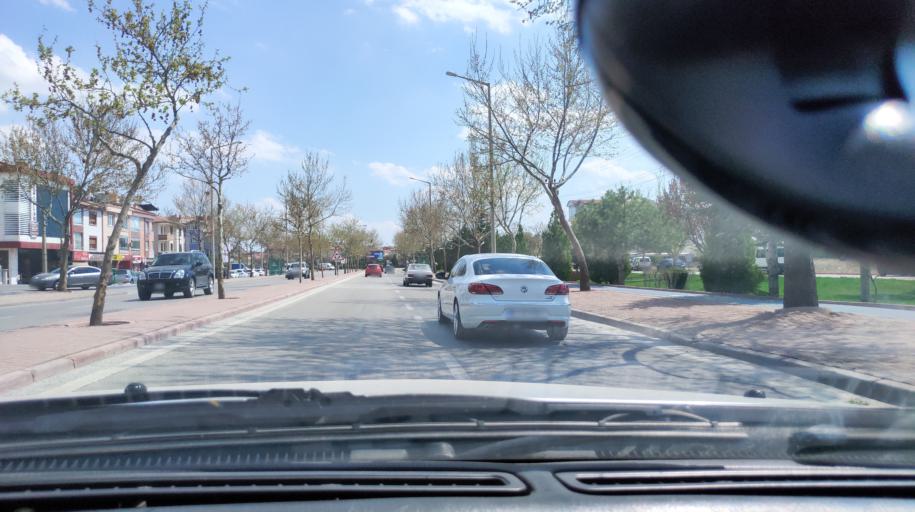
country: TR
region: Konya
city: Selcuklu
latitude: 37.9280
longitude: 32.4945
